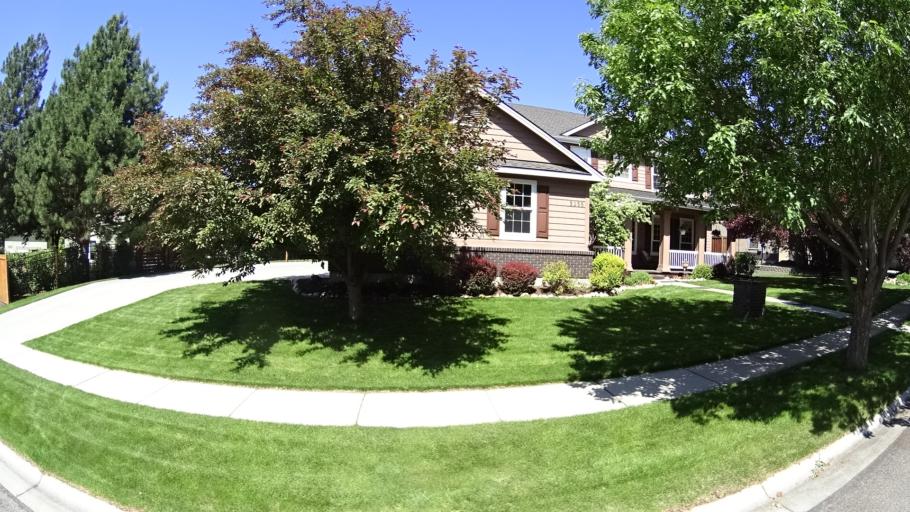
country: US
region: Idaho
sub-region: Ada County
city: Boise
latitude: 43.5722
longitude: -116.1148
